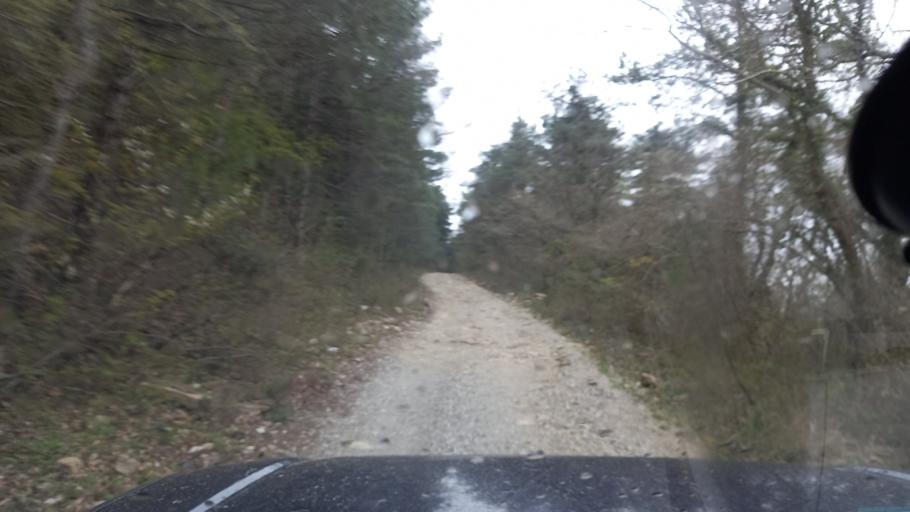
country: RU
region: Krasnodarskiy
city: Arkhipo-Osipovka
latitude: 44.3719
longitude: 38.4515
